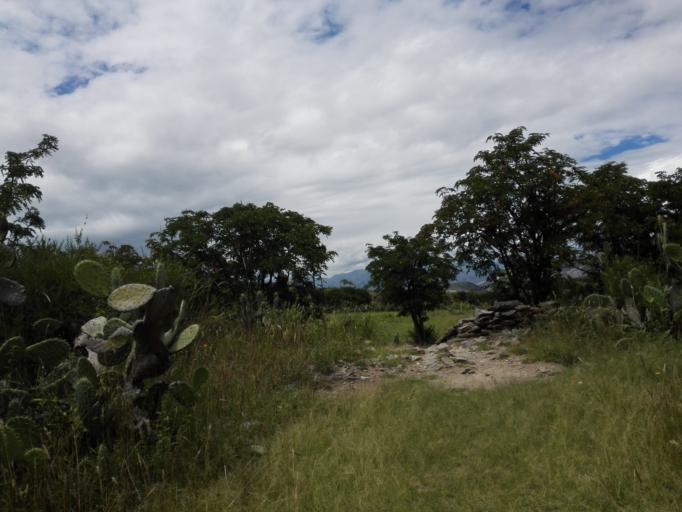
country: PE
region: Ayacucho
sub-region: Provincia de Huamanga
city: Pacaycasa
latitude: -13.0592
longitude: -74.1981
